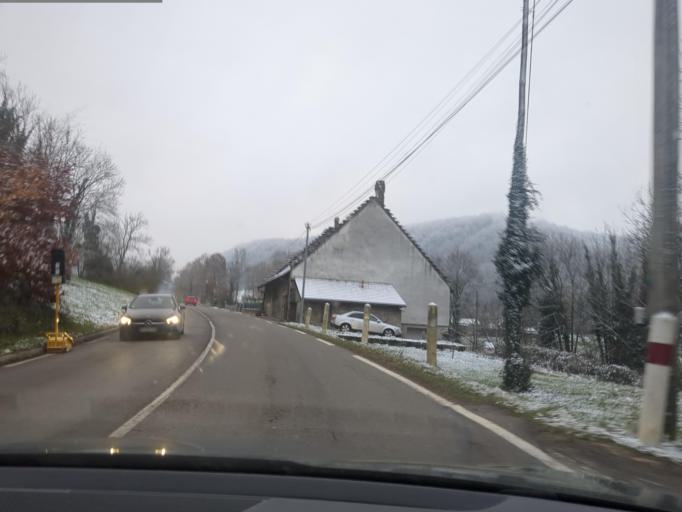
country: FR
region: Franche-Comte
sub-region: Departement du Jura
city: Perrigny
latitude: 46.6412
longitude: 5.6017
